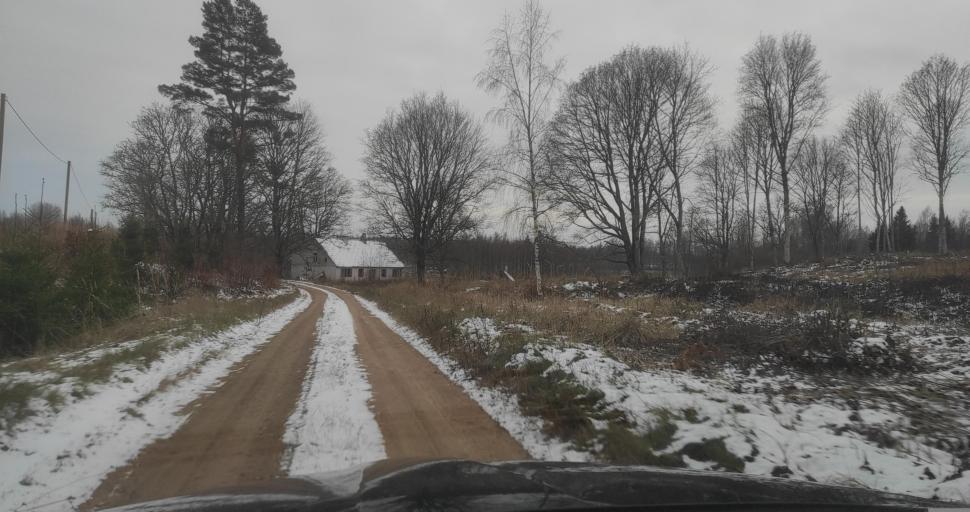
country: LV
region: Alsunga
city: Alsunga
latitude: 56.9590
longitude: 21.6424
